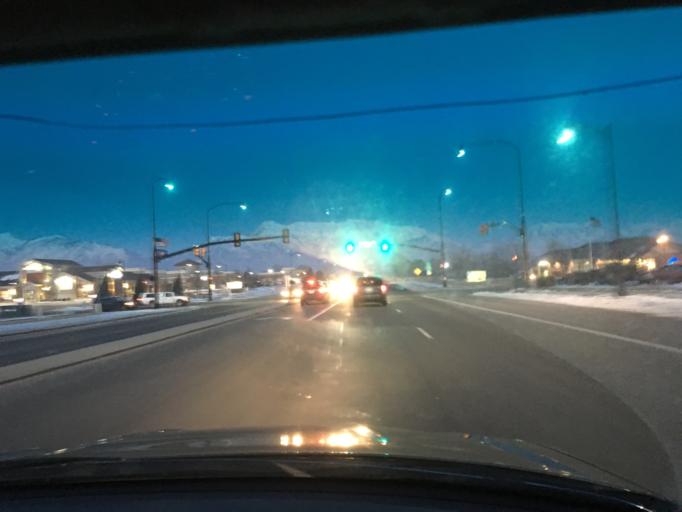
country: US
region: Utah
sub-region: Utah County
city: Saratoga Springs
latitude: 40.3875
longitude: -111.9137
